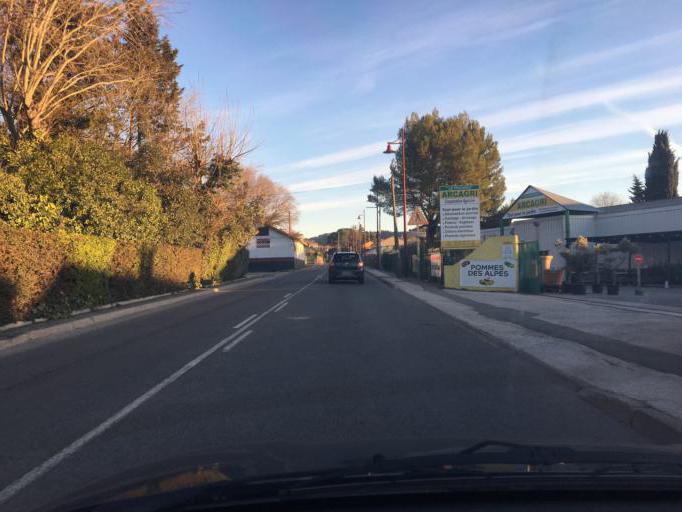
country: FR
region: Provence-Alpes-Cote d'Azur
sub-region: Departement du Var
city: Les Arcs
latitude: 43.4518
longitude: 6.4777
